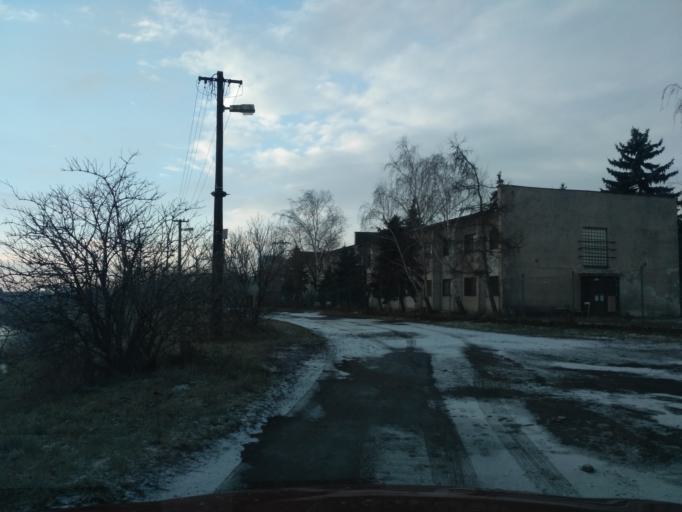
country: SK
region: Kosicky
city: Kosice
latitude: 48.7279
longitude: 21.2707
